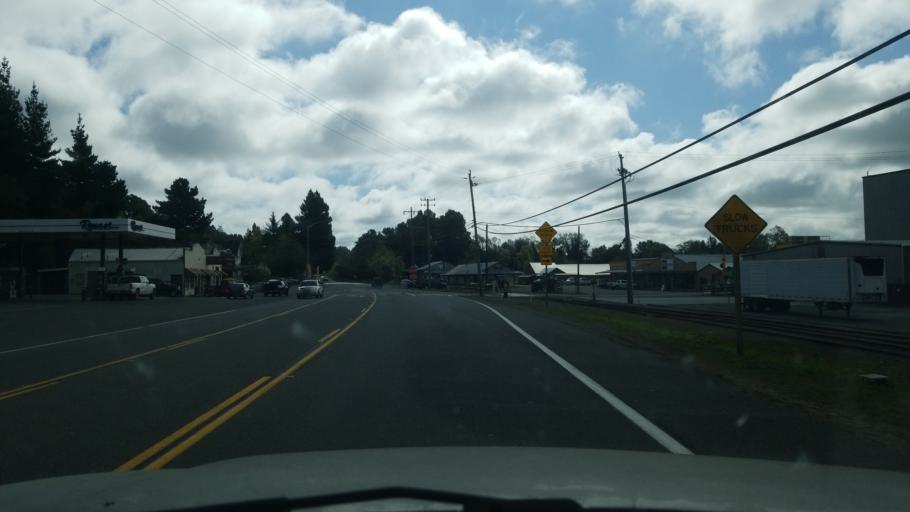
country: US
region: California
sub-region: Humboldt County
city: Fortuna
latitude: 40.6167
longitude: -124.2027
